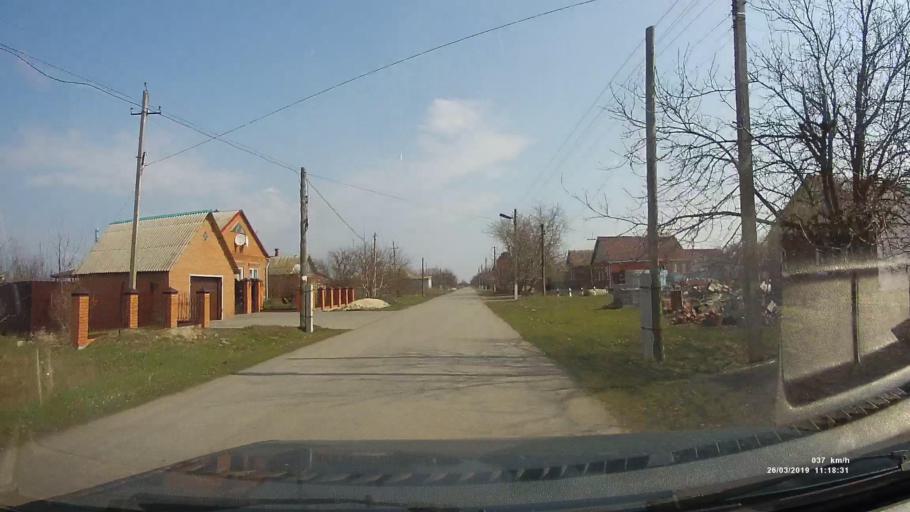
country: RU
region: Krasnodarskiy
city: Shabel'skoye
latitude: 47.1327
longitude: 38.5335
